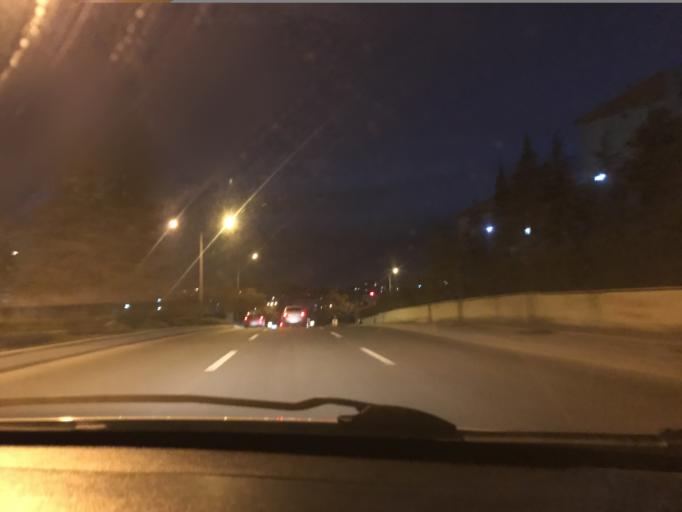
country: TR
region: Ankara
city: Batikent
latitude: 39.9605
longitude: 32.7310
